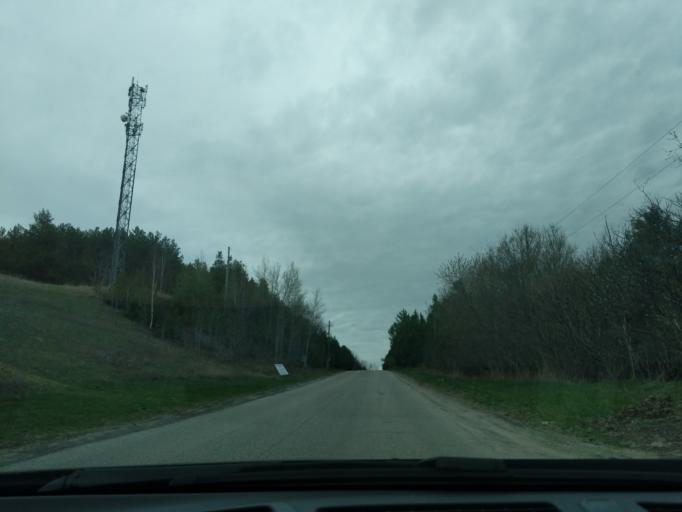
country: CA
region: Ontario
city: Orangeville
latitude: 44.0170
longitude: -79.9682
